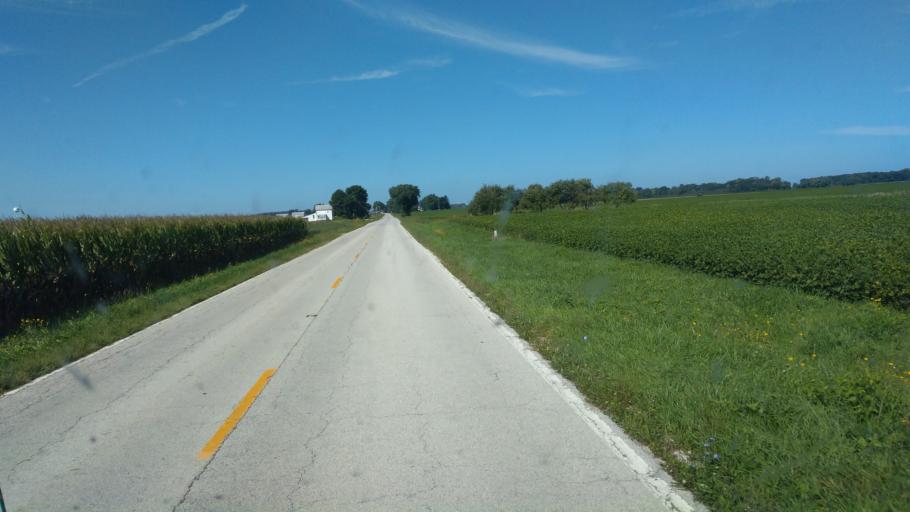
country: US
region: Ohio
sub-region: Ottawa County
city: Port Clinton
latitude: 41.3976
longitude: -82.8920
